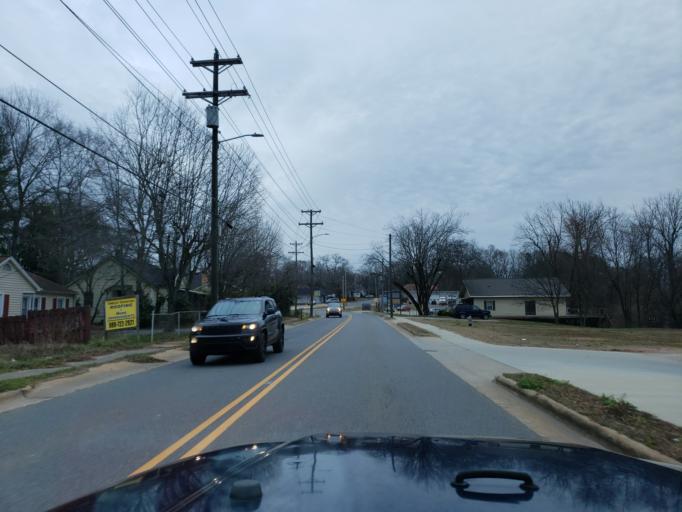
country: US
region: North Carolina
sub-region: Cleveland County
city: Shelby
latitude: 35.3010
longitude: -81.5458
